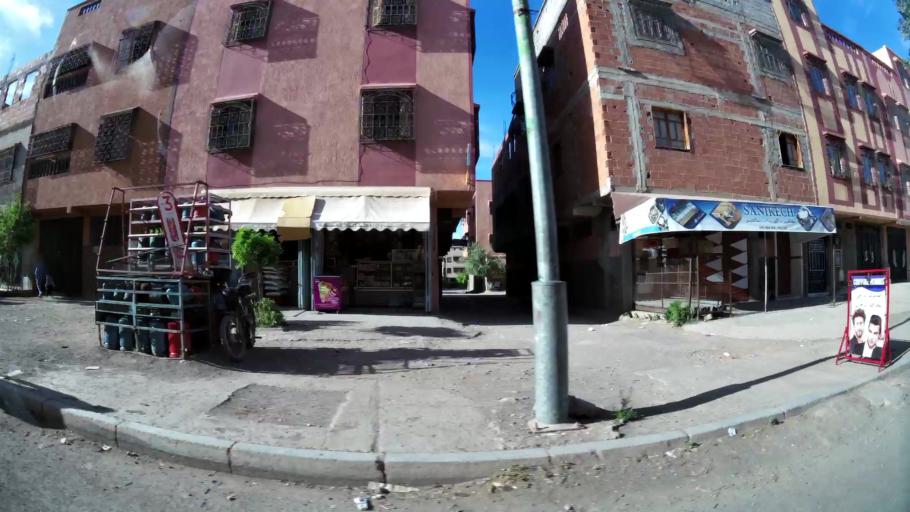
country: MA
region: Marrakech-Tensift-Al Haouz
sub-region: Marrakech
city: Marrakesh
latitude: 31.6880
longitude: -8.0674
